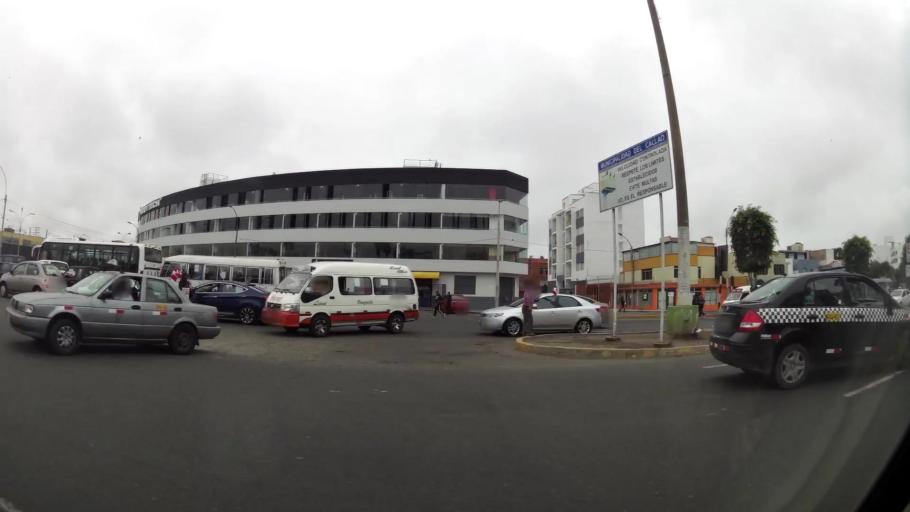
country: PE
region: Callao
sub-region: Callao
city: Callao
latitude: -12.0628
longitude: -77.0980
